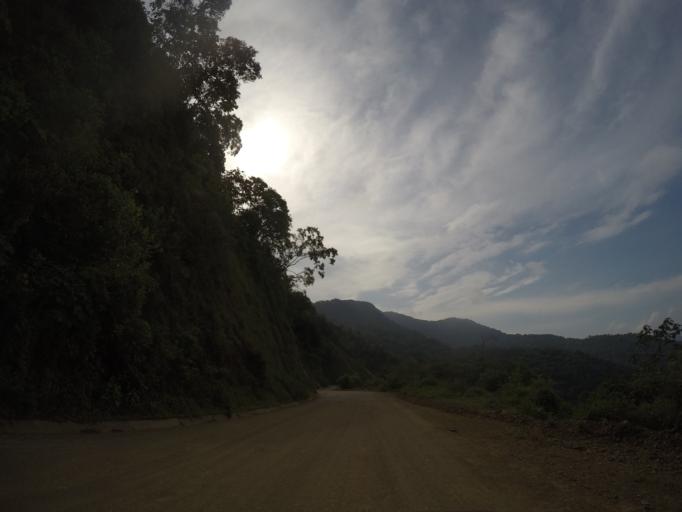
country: MX
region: Oaxaca
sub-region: San Pedro Pochutla
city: Los Naranjos Esquipulas
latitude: 15.9586
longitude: -96.4555
